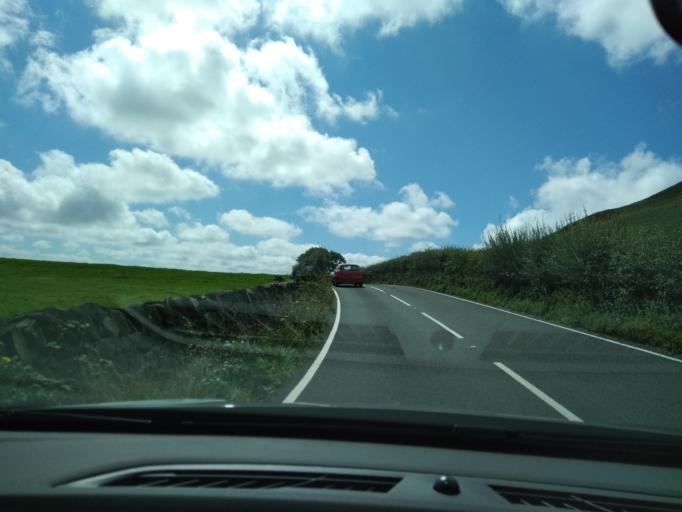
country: GB
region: England
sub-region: Cumbria
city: Millom
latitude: 54.2399
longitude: -3.3205
